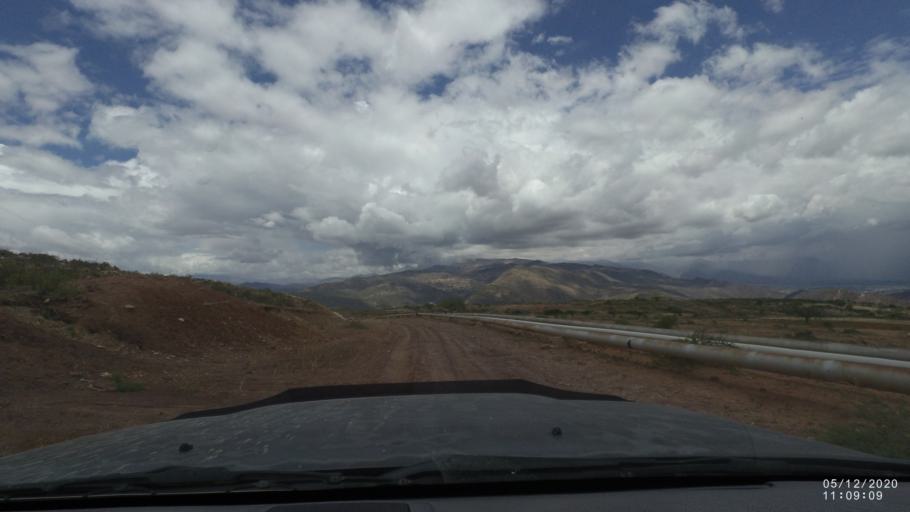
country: BO
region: Cochabamba
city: Sipe Sipe
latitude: -17.5499
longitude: -66.3164
